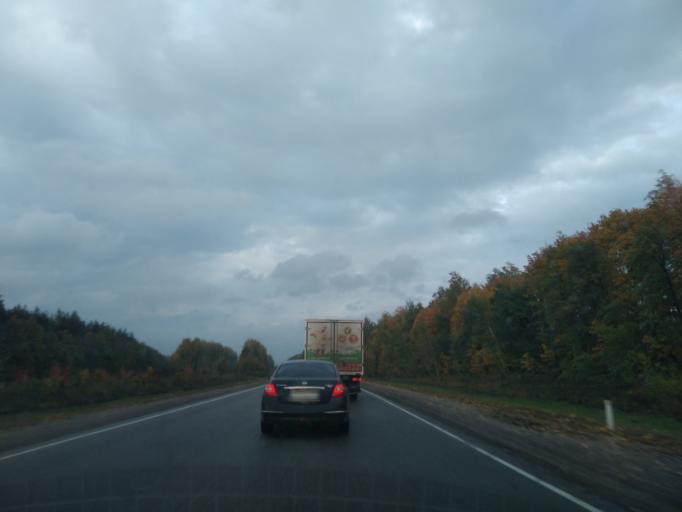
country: RU
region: Lipetsk
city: Borinskoye
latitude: 52.5752
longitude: 39.2113
